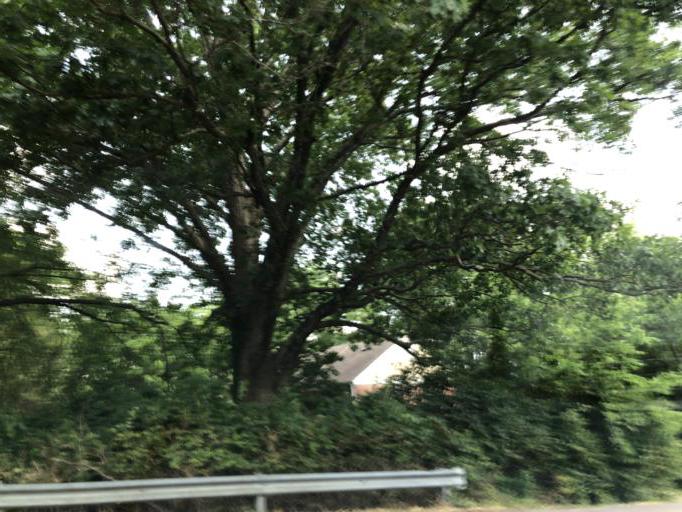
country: US
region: Tennessee
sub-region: Davidson County
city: Goodlettsville
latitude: 36.2465
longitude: -86.7195
